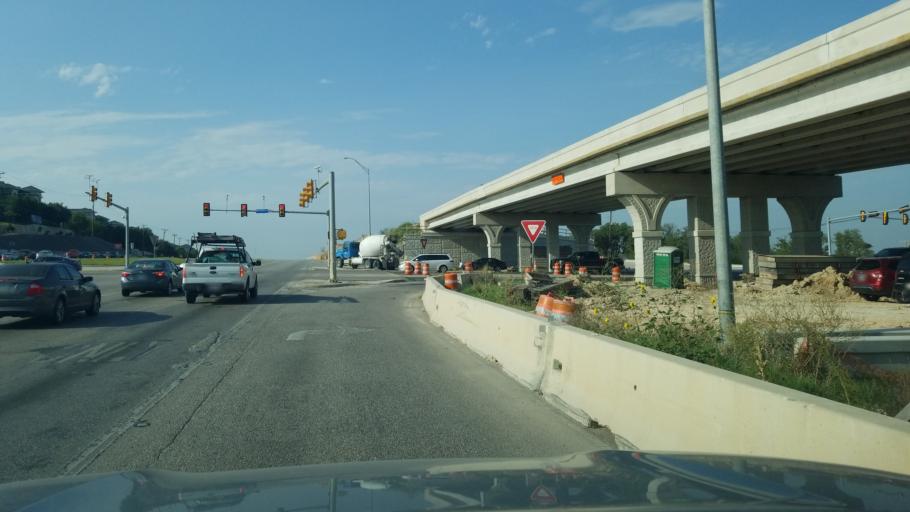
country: US
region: Texas
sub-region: Bexar County
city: Leon Valley
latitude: 29.4659
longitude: -98.7113
